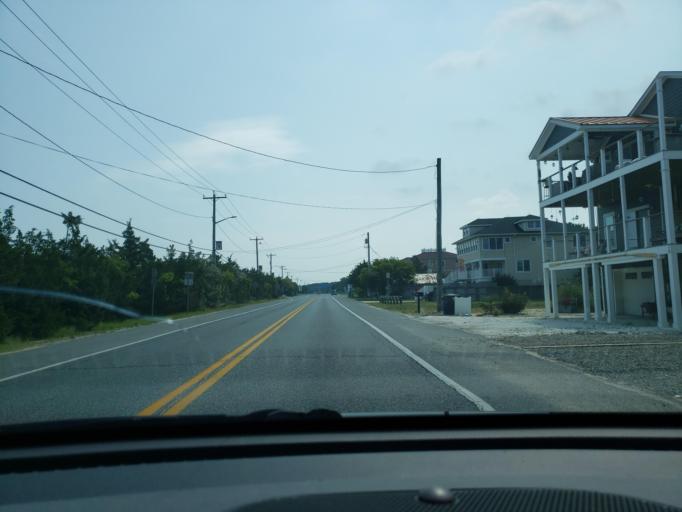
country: US
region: Delaware
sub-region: Sussex County
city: Lewes
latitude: 38.7804
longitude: -75.1295
